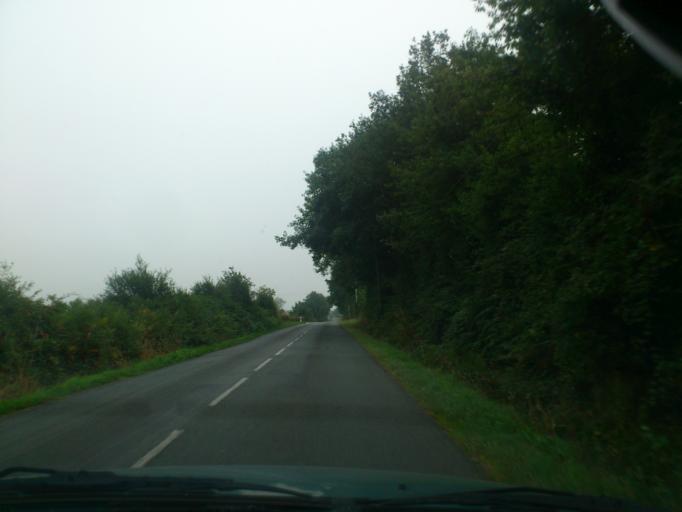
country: FR
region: Pays de la Loire
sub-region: Departement de la Vendee
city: Saint-Hilaire-de-Loulay
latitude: 46.9880
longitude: -1.3604
